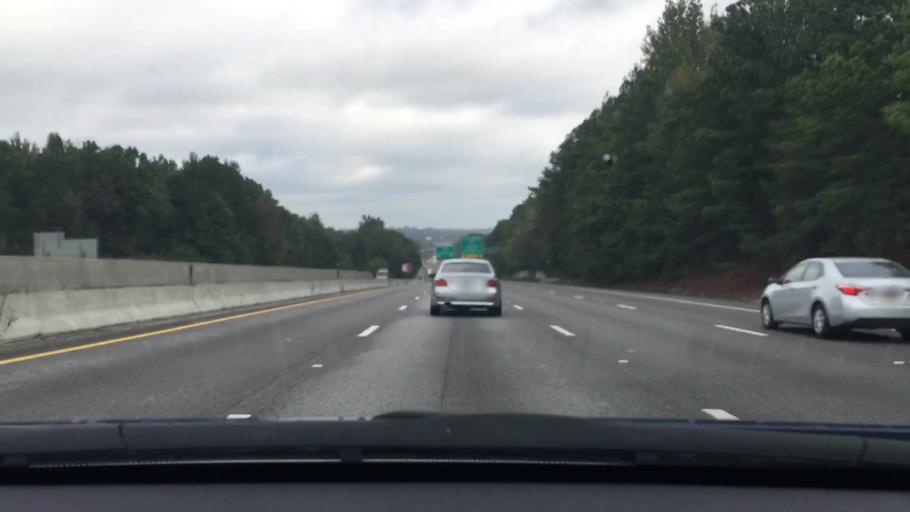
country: US
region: South Carolina
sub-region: Lexington County
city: Saint Andrews
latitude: 34.0110
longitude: -81.1097
